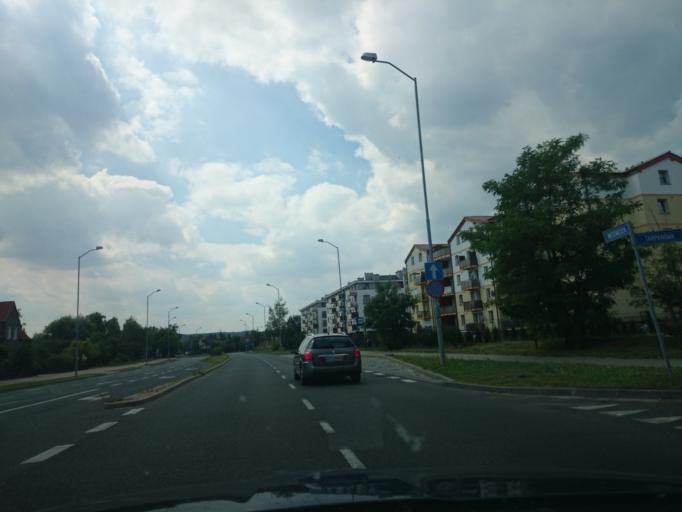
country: PL
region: West Pomeranian Voivodeship
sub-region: Powiat gryfinski
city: Stare Czarnowo
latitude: 53.3761
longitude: 14.6894
